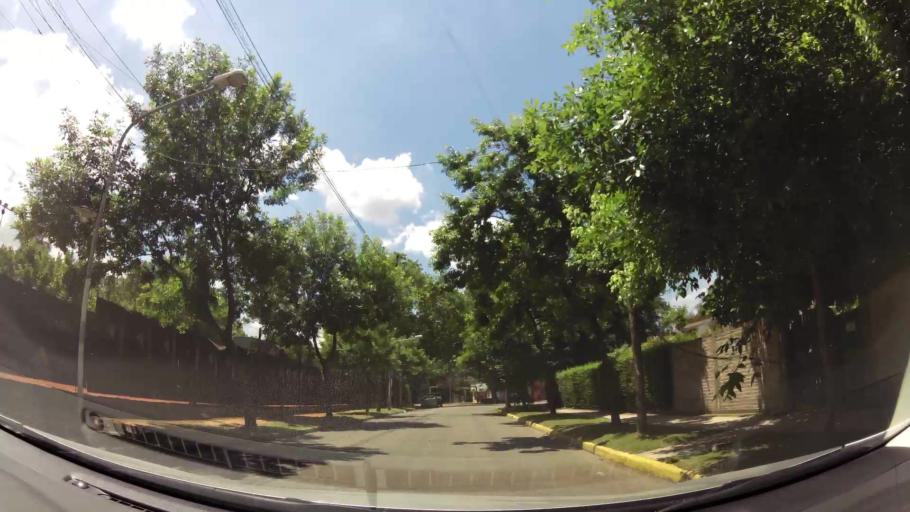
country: AR
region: Buenos Aires
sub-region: Partido de Tigre
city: Tigre
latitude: -34.4144
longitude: -58.5864
